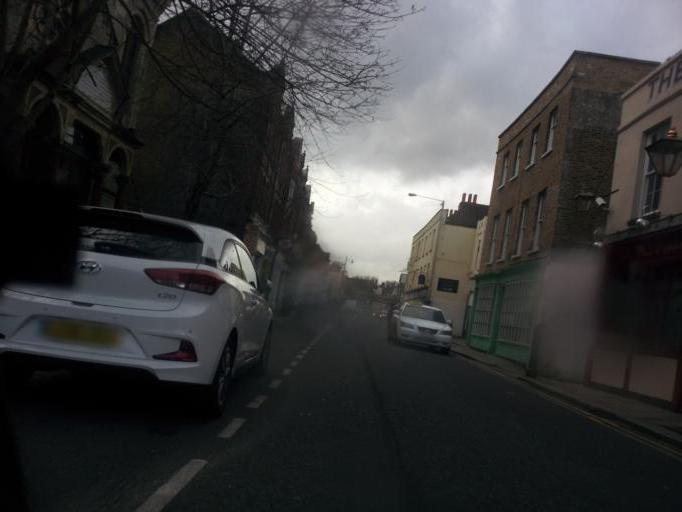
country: GB
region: England
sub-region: Medway
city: Rochester
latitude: 51.3833
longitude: 0.5155
